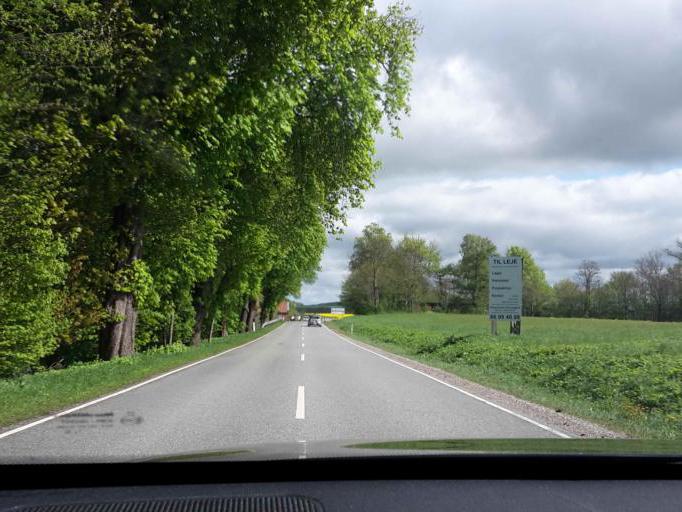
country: DK
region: Central Jutland
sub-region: Syddjurs Kommune
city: Hornslet
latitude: 56.3314
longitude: 10.3318
